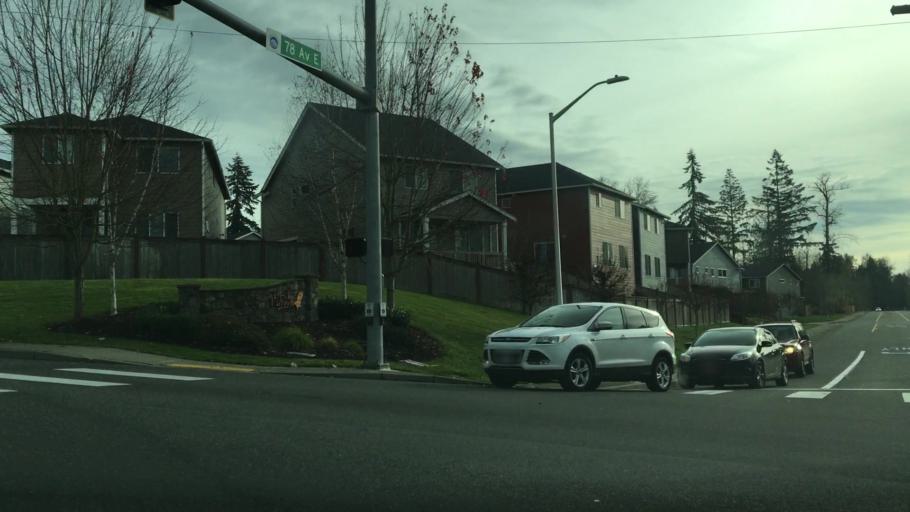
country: US
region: Washington
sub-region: Pierce County
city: Frederickson
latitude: 47.1112
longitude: -122.3254
